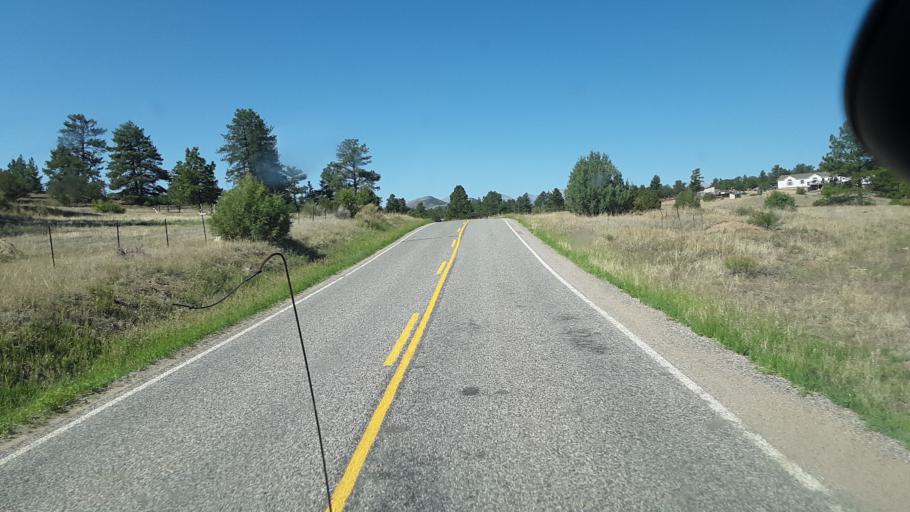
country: US
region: Colorado
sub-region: Fremont County
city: Canon City
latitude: 38.3681
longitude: -105.4610
